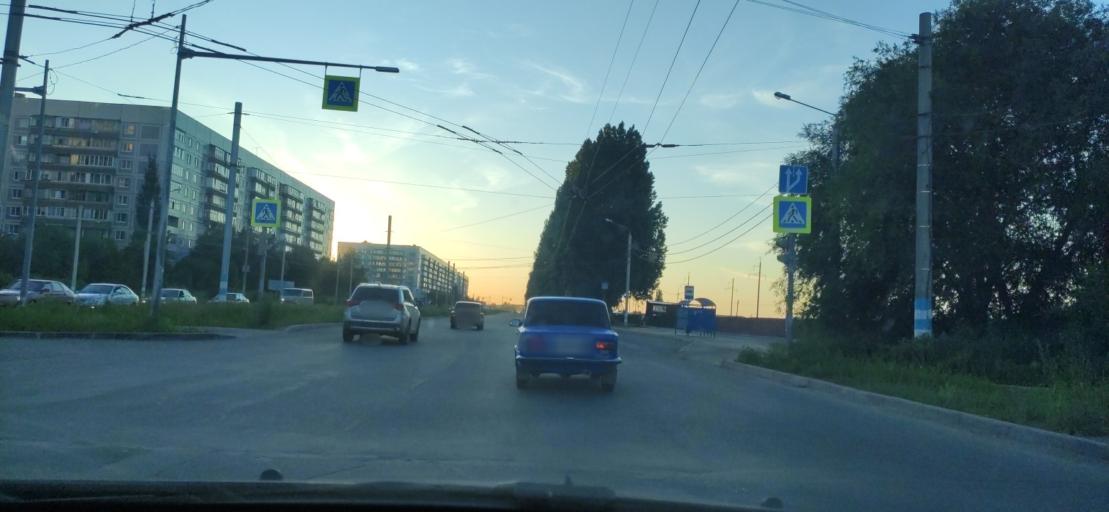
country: RU
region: Ulyanovsk
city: Mirnyy
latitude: 54.3822
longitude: 48.6206
